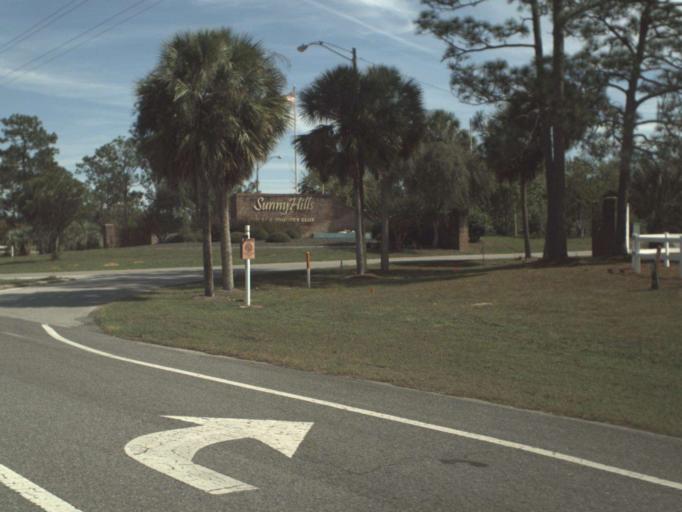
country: US
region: Florida
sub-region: Holmes County
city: Bonifay
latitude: 30.5525
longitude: -85.6279
